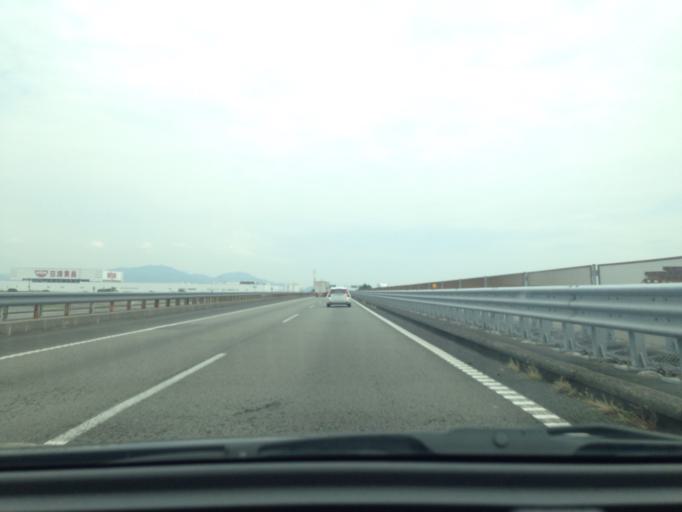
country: JP
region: Shizuoka
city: Fujieda
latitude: 34.8036
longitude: 138.2490
